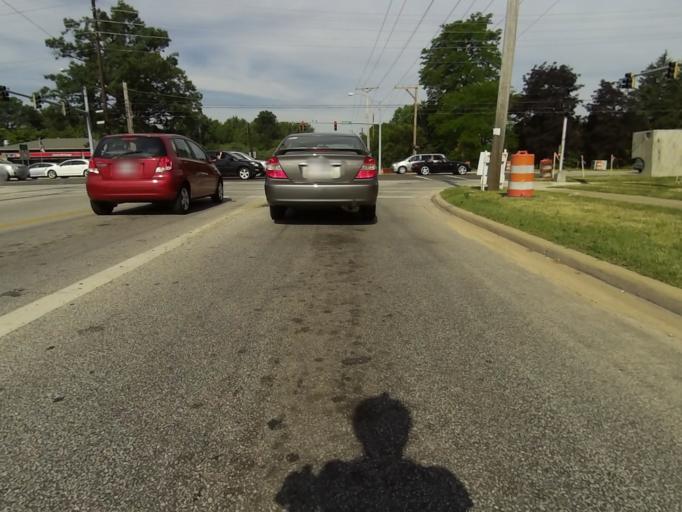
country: US
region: Ohio
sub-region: Summit County
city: Hudson
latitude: 41.2029
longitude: -81.4401
